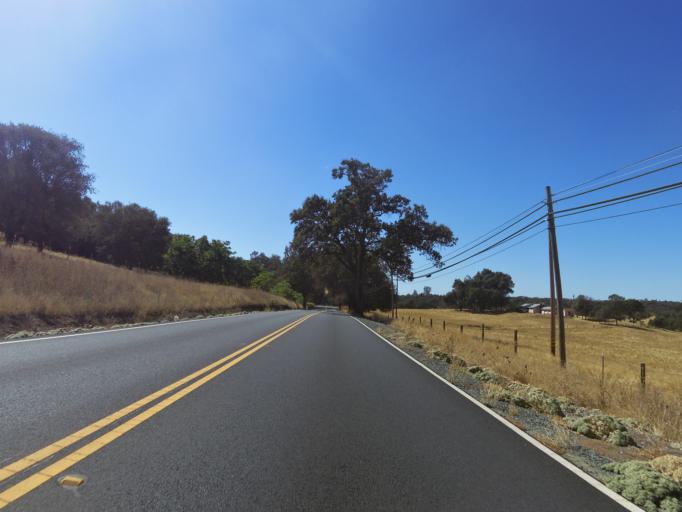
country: US
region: California
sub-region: El Dorado County
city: Deer Park
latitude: 38.6759
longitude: -120.8503
